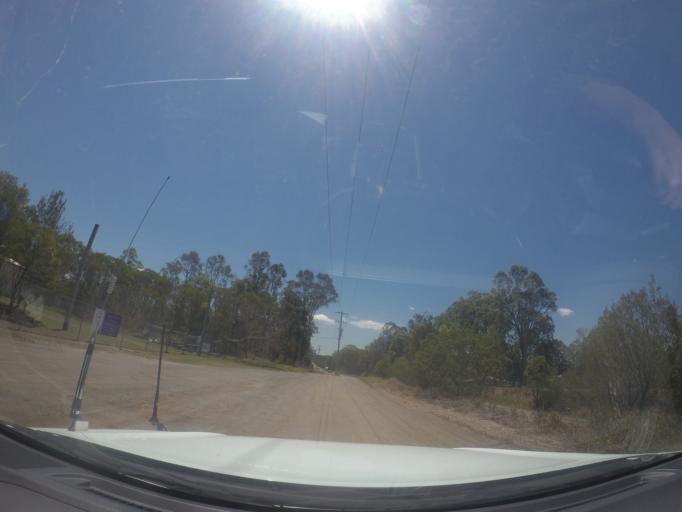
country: AU
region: Queensland
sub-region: Logan
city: Logan Reserve
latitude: -27.7416
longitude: 153.1269
